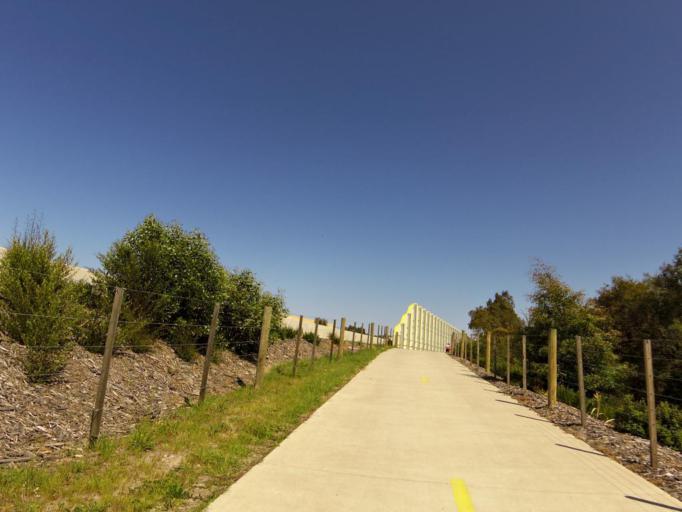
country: AU
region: Victoria
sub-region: Banyule
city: Bundoora
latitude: -37.6873
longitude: 145.0424
